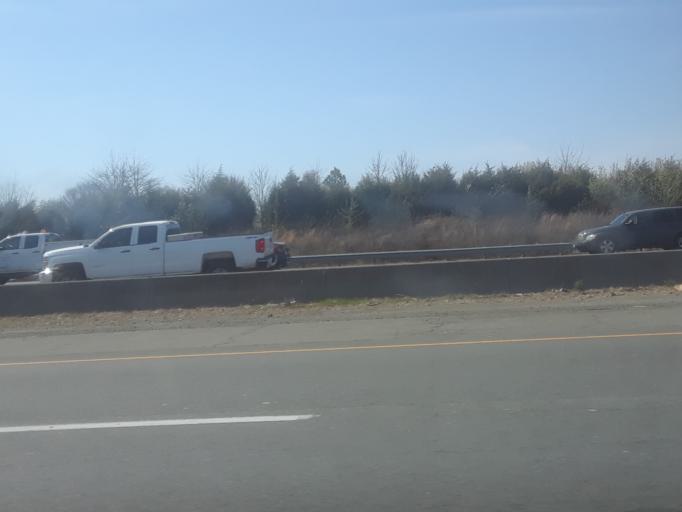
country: US
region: Virginia
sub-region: Fairfax County
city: Chantilly
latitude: 38.8883
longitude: -77.4454
